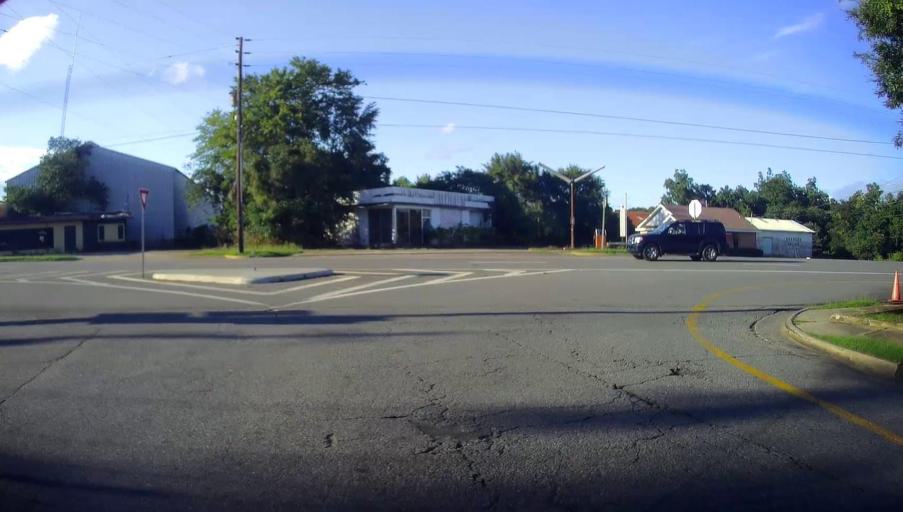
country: US
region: Georgia
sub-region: Pulaski County
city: Hawkinsville
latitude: 32.2848
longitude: -83.4631
